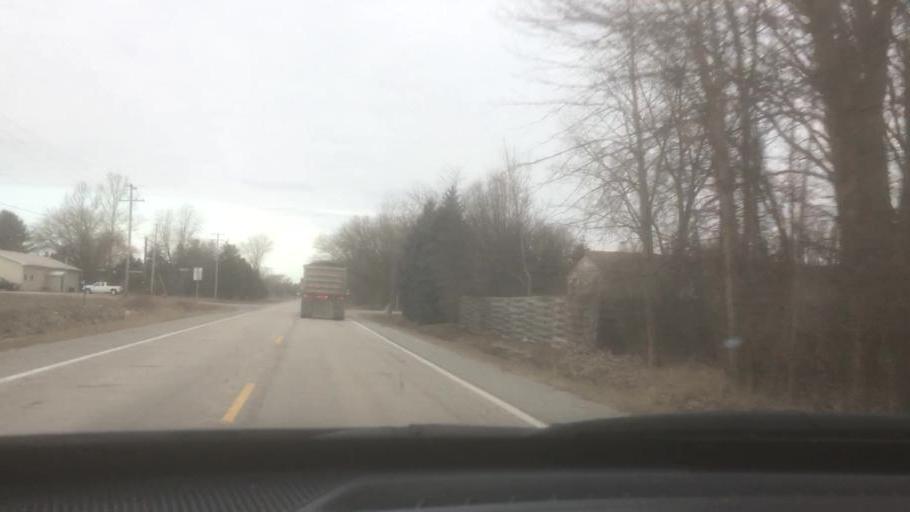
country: US
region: Michigan
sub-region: Bay County
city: Essexville
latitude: 43.5221
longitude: -83.7969
